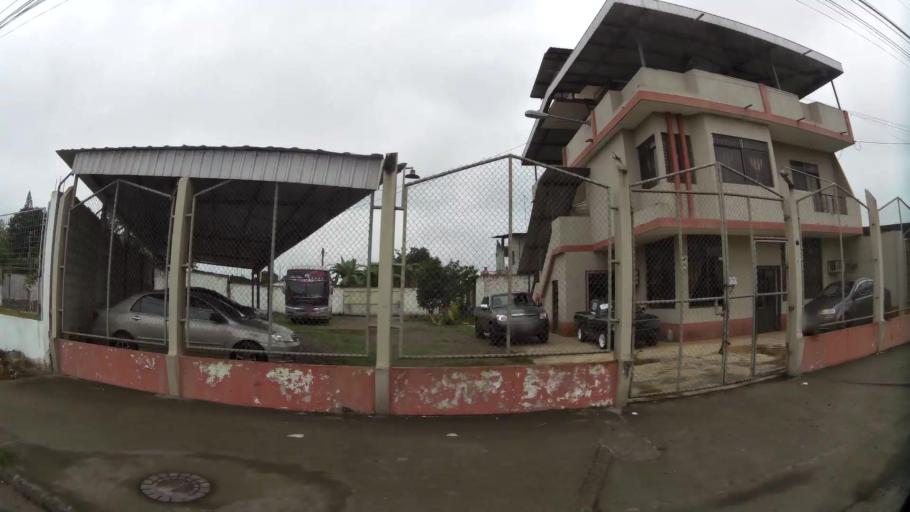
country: EC
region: El Oro
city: Pasaje
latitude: -3.3271
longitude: -79.8201
